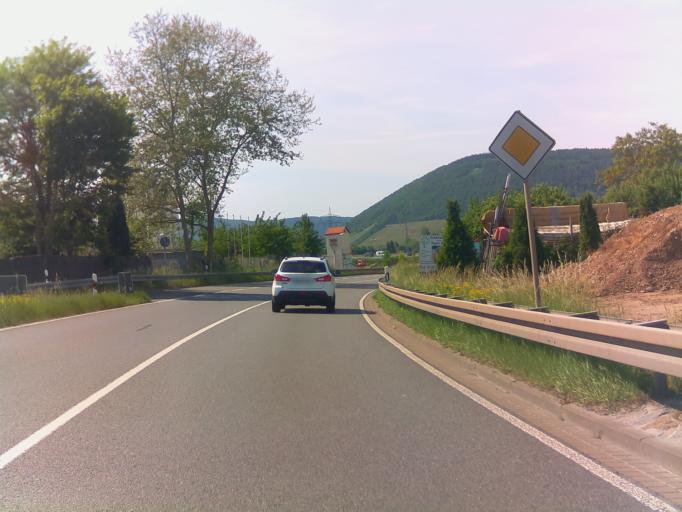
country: DE
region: Bavaria
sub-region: Regierungsbezirk Unterfranken
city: Grossheubach
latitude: 49.7164
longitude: 9.2330
